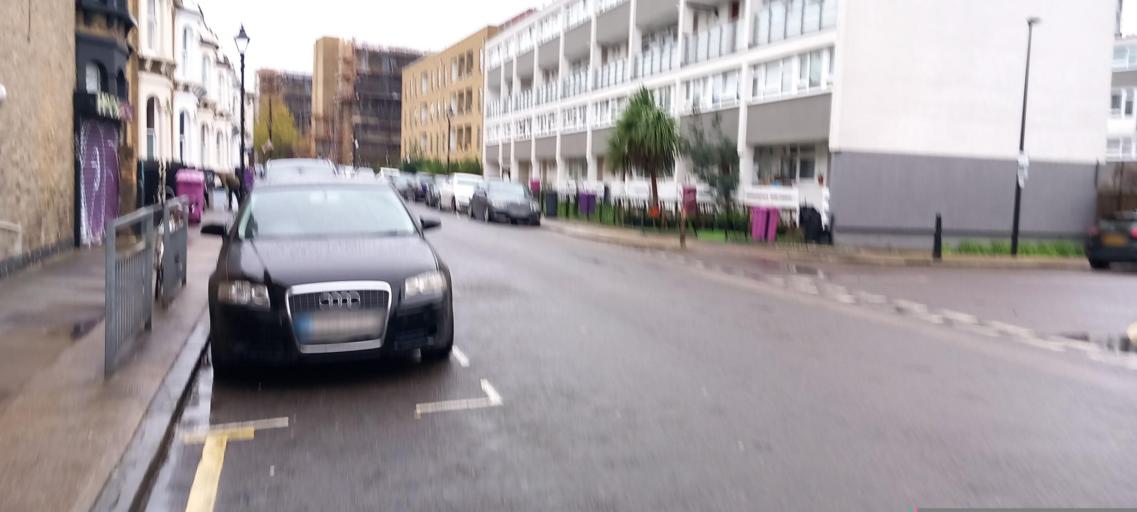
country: GB
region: England
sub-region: Greater London
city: Poplar
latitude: 51.5223
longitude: -0.0328
